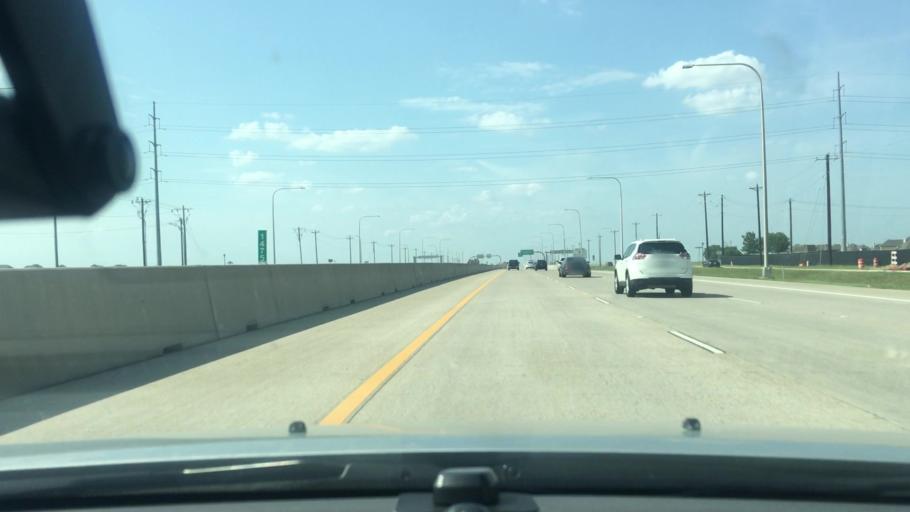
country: US
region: Texas
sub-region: Collin County
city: Frisco
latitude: 33.1812
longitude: -96.8393
